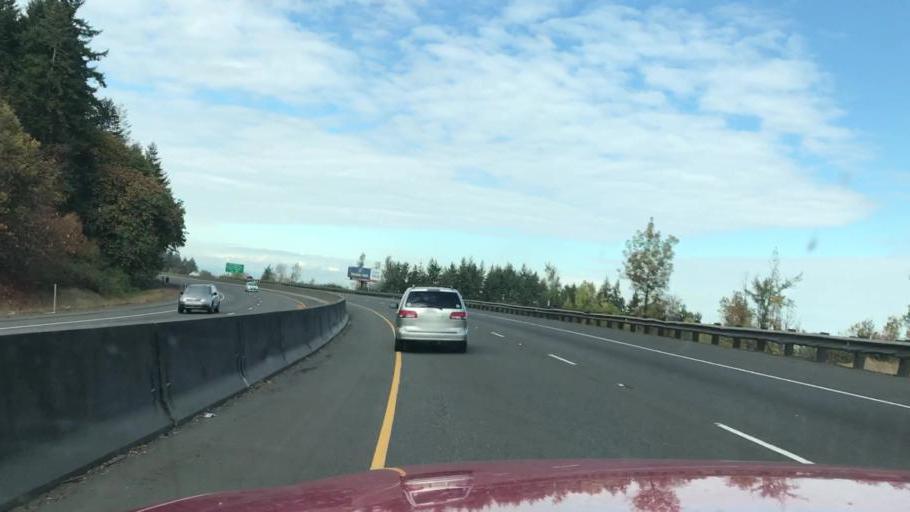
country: US
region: Oregon
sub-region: Lane County
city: Springfield
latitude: 44.0333
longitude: -123.0321
